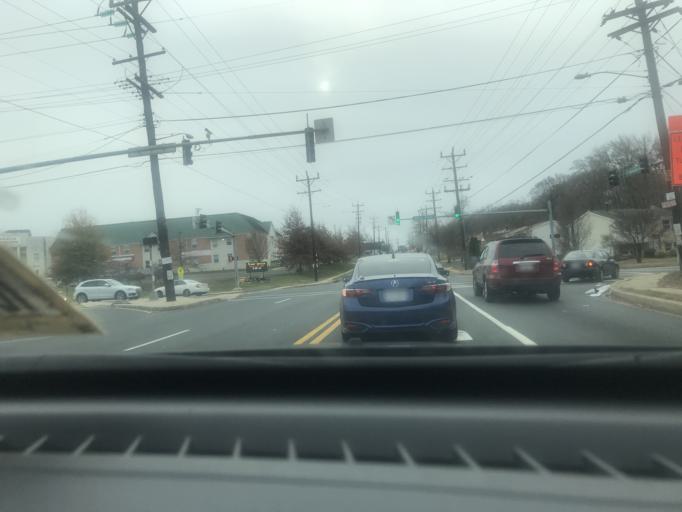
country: US
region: Maryland
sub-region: Prince George's County
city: Oxon Hill
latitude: 38.8004
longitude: -76.9799
